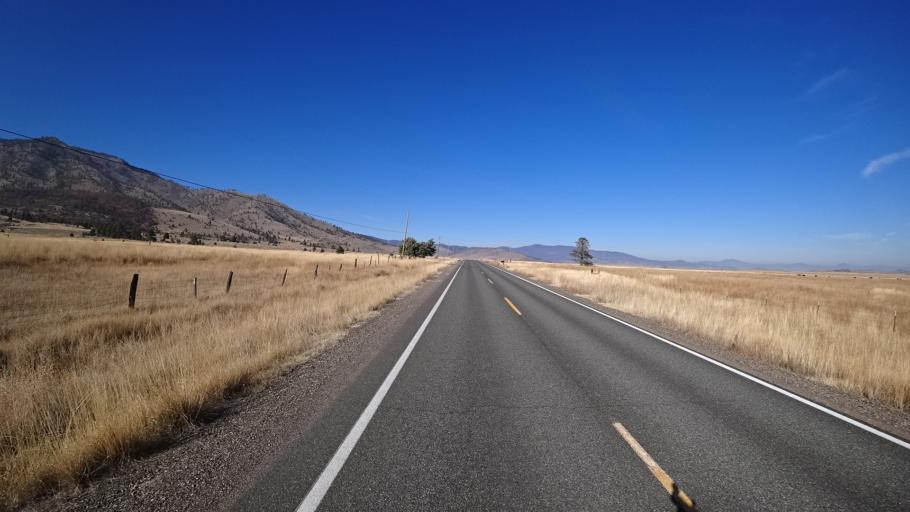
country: US
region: California
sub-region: Siskiyou County
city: Weed
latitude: 41.4743
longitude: -122.4848
